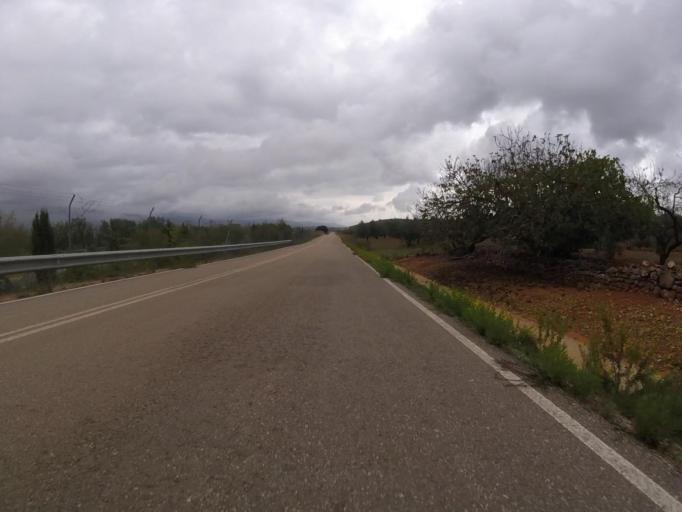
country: ES
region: Valencia
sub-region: Provincia de Castello
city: Cabanes
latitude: 40.1751
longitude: 0.0445
